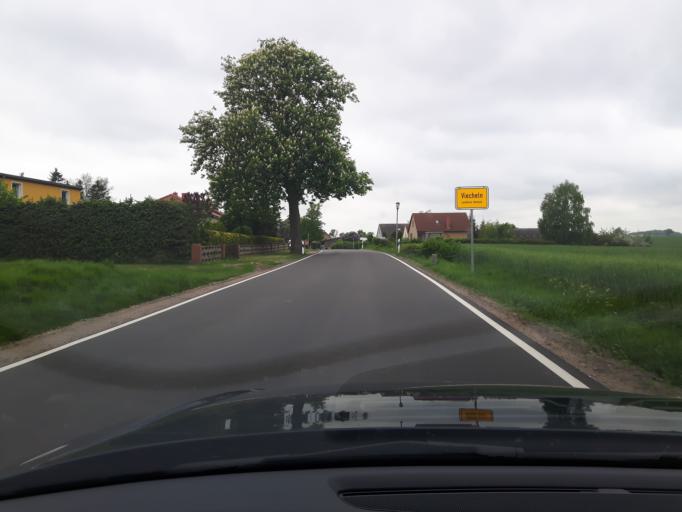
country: DE
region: Mecklenburg-Vorpommern
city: Gnoien
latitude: 54.0136
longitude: 12.6607
